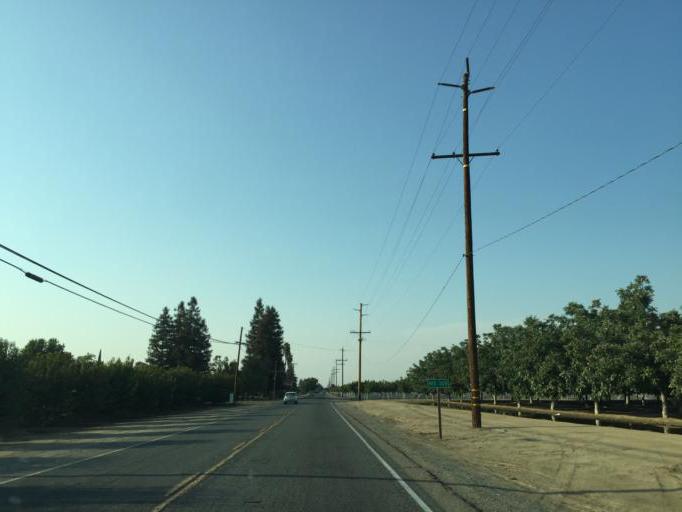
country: US
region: California
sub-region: Tulare County
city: Ivanhoe
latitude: 36.3699
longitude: -119.2519
